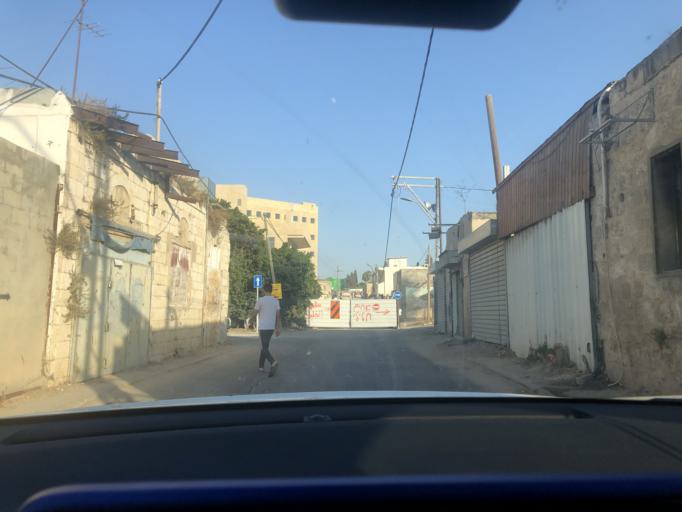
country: IL
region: Central District
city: Lod
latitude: 31.9553
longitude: 34.8962
